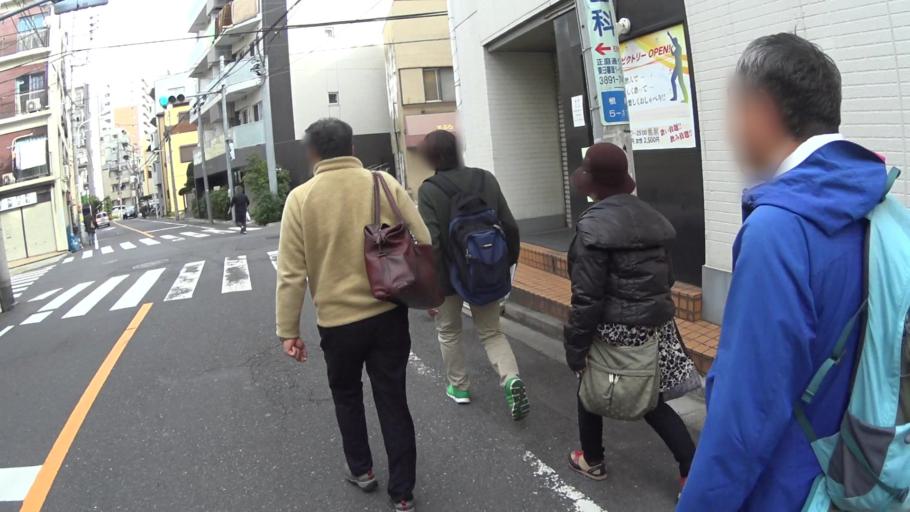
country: JP
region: Saitama
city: Soka
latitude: 35.7287
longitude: 139.7897
